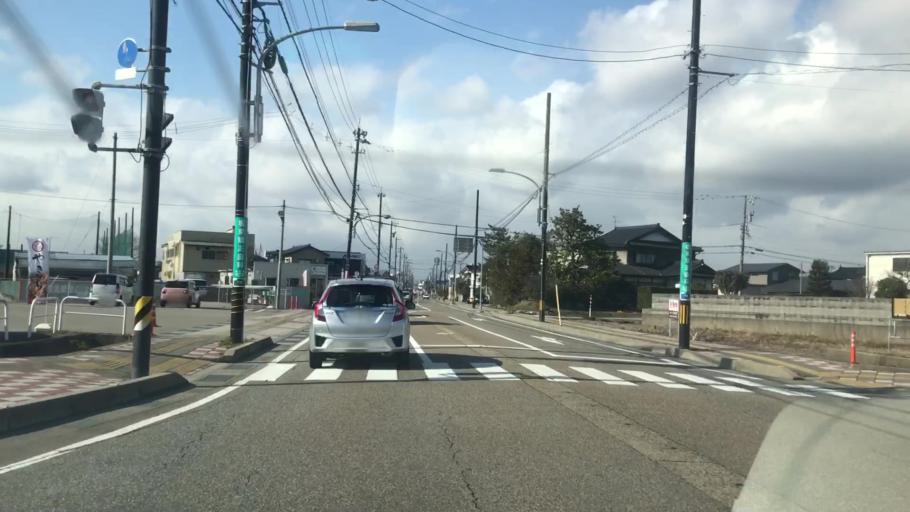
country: JP
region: Toyama
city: Takaoka
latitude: 36.7281
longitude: 137.0598
